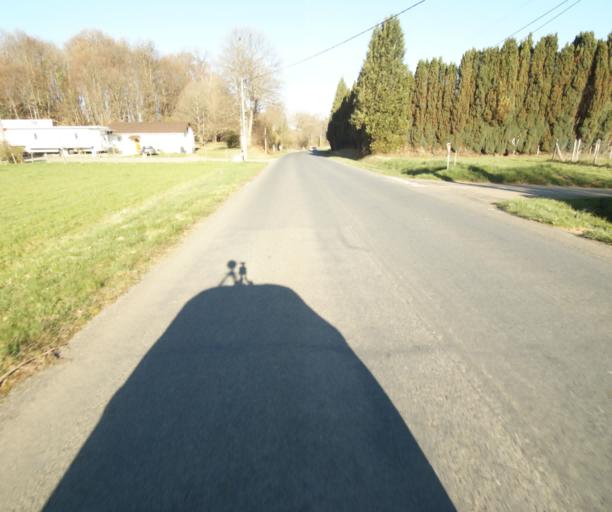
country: FR
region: Limousin
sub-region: Departement de la Correze
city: Uzerche
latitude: 45.3880
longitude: 1.6011
